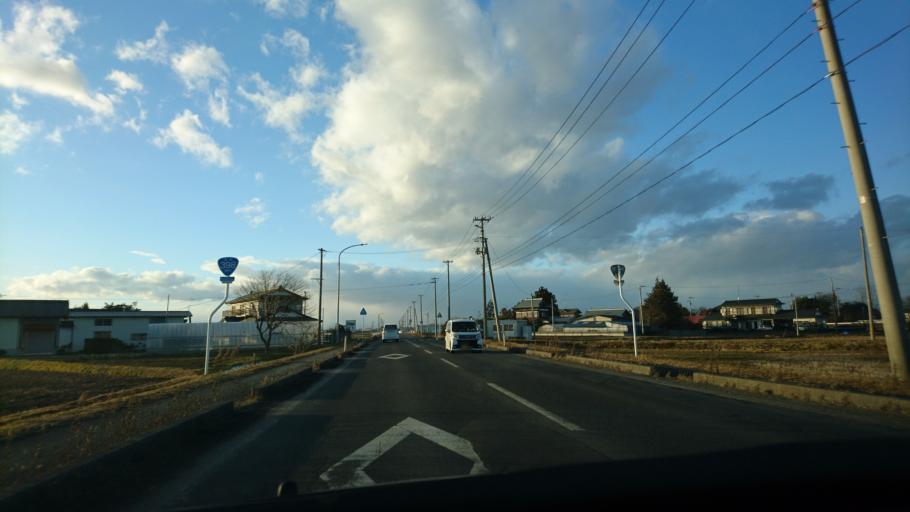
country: JP
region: Miyagi
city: Wakuya
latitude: 38.7147
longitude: 141.1683
